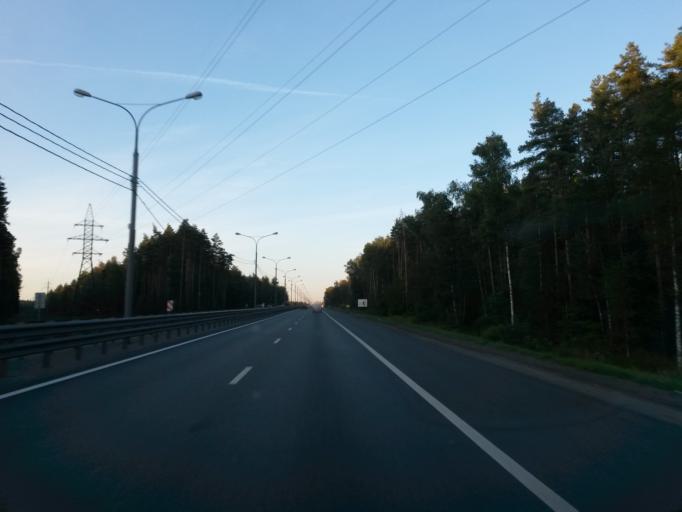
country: RU
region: Moskovskaya
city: Kostino
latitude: 56.0345
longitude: 37.8891
